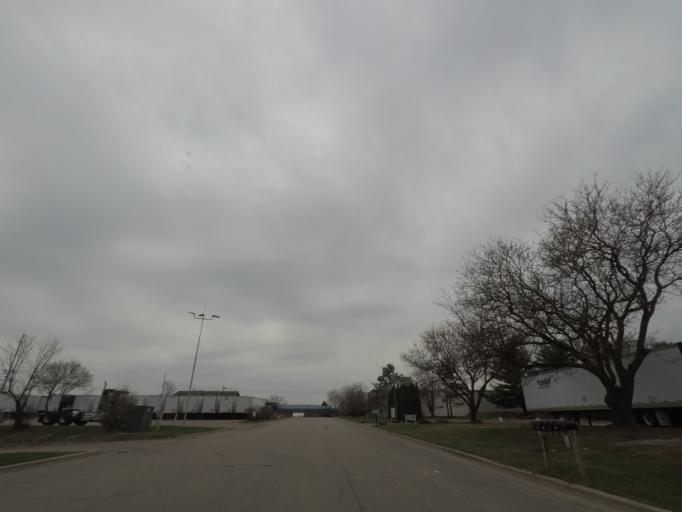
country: US
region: Wisconsin
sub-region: Dane County
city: Middleton
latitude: 43.0993
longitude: -89.5322
